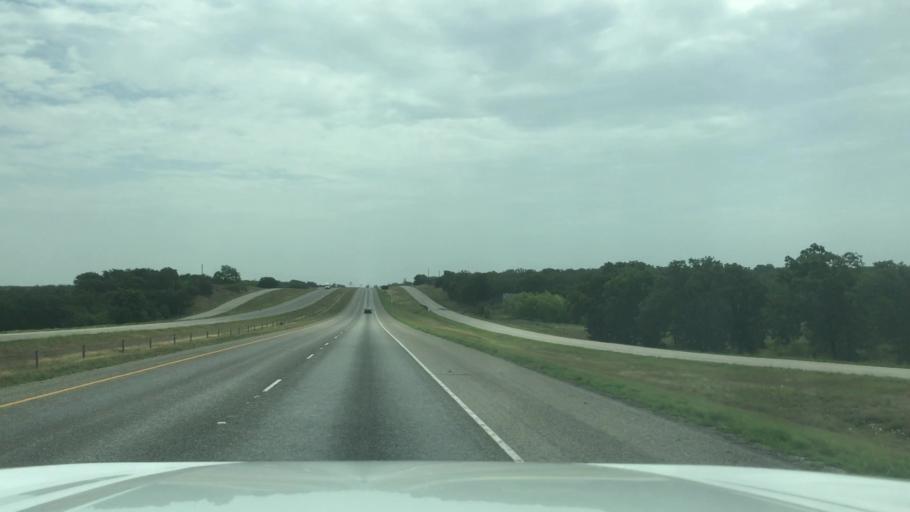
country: US
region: Texas
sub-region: Eastland County
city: Cisco
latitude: 32.3754
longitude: -99.0337
